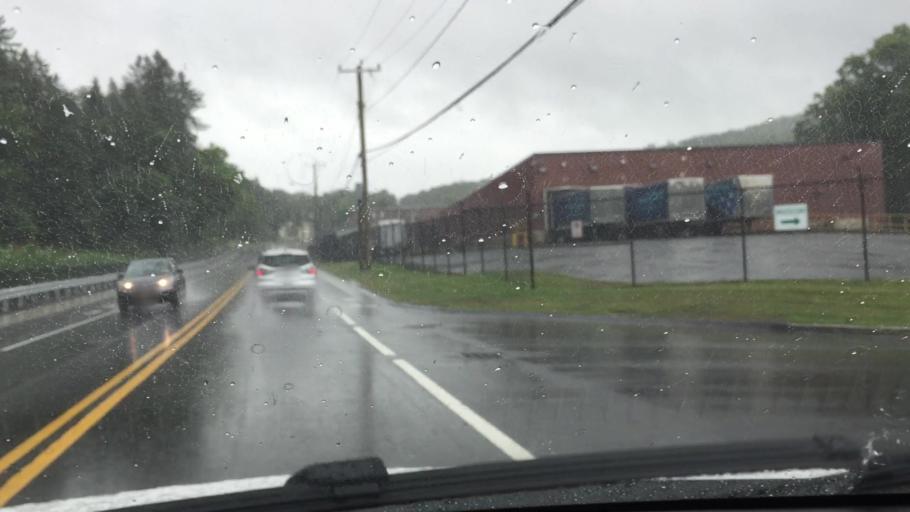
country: US
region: Massachusetts
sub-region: Berkshire County
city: Dalton
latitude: 42.4716
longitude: -73.1760
